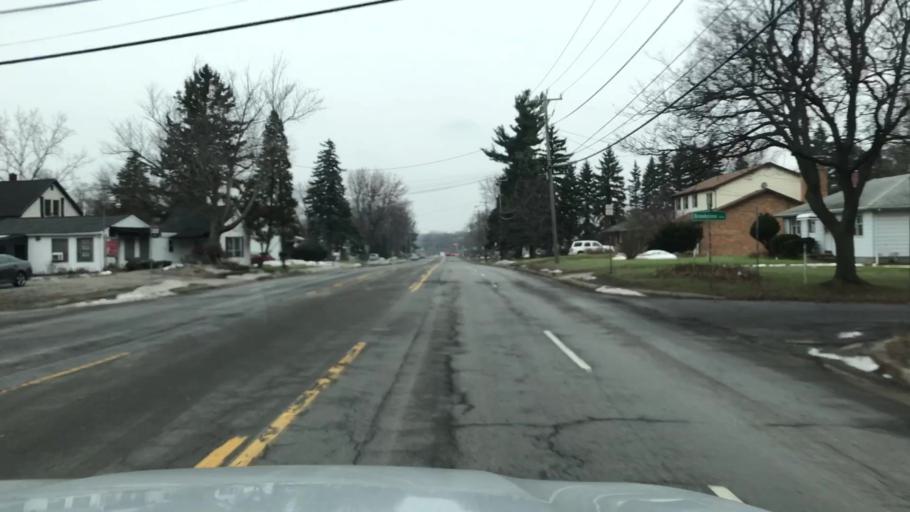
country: US
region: New York
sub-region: Erie County
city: Blasdell
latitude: 42.7851
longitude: -78.7907
